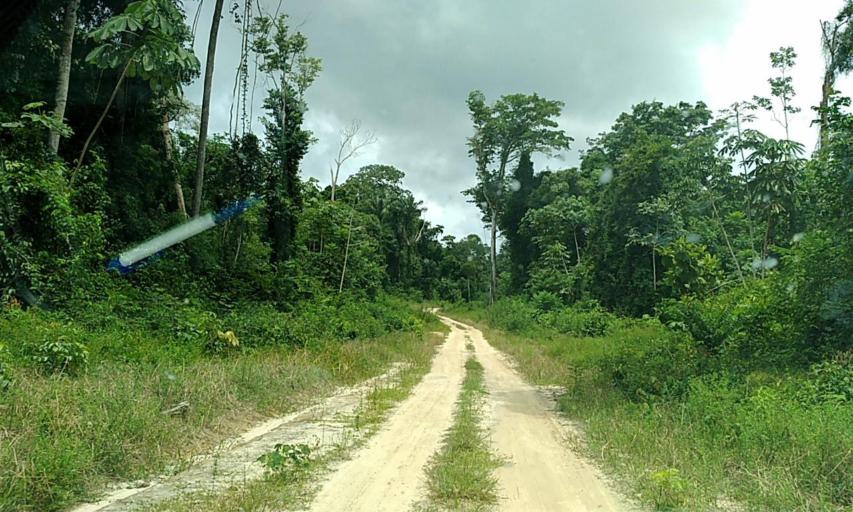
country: BR
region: Para
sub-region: Altamira
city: Altamira
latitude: -3.0637
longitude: -52.9087
